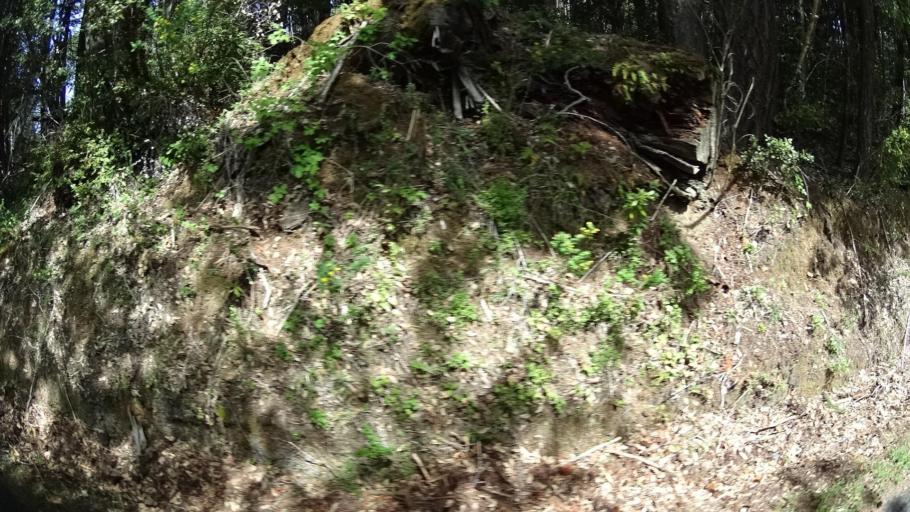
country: US
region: California
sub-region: Humboldt County
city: Redway
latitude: 40.3655
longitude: -123.7301
